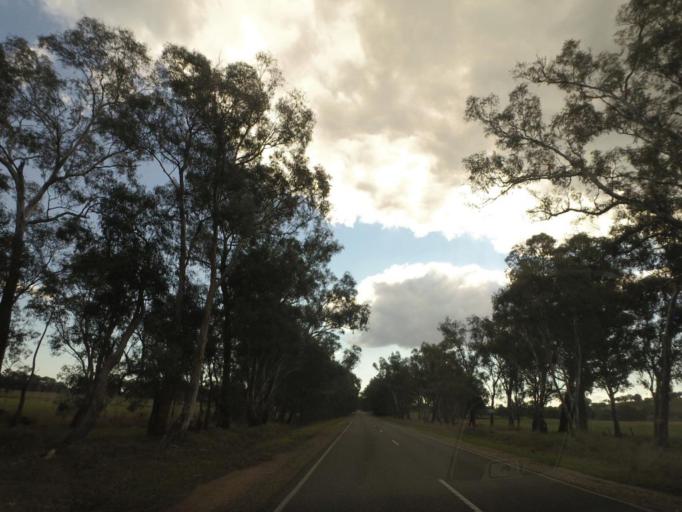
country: AU
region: New South Wales
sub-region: Corowa Shire
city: Howlong
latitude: -36.1904
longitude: 146.6136
